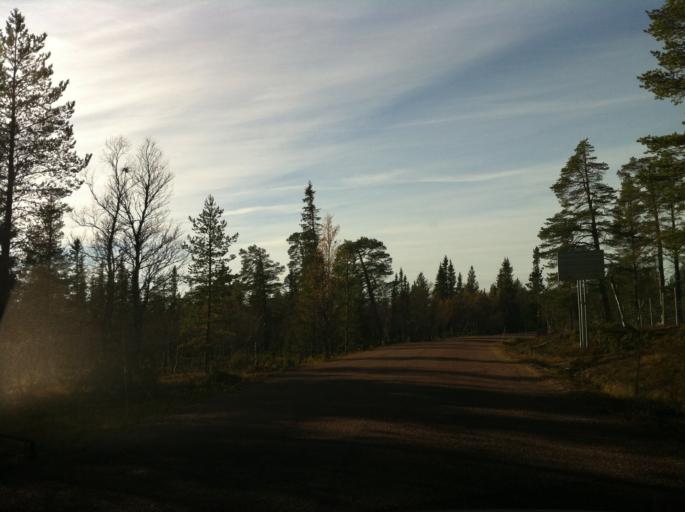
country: NO
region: Hedmark
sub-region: Engerdal
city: Engerdal
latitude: 62.0633
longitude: 12.2485
